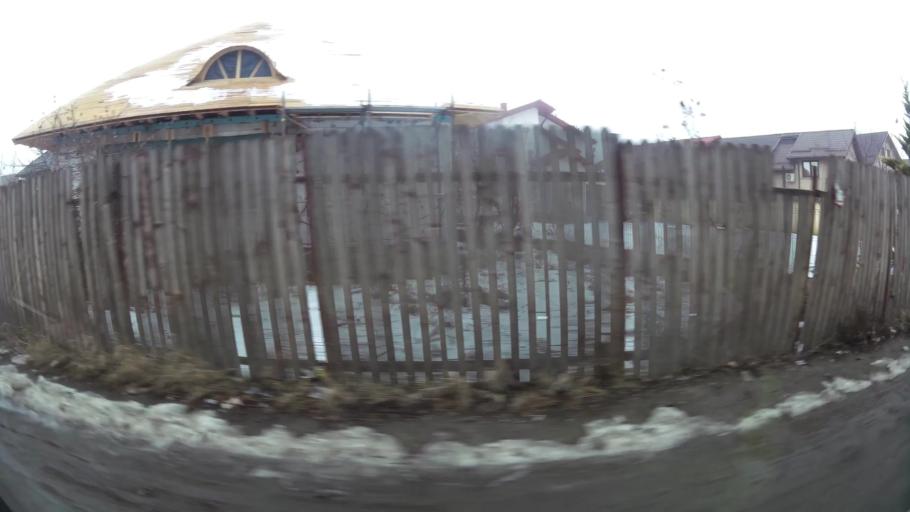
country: RO
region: Ilfov
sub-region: Comuna Chiajna
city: Rosu
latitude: 44.4512
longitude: 25.9934
